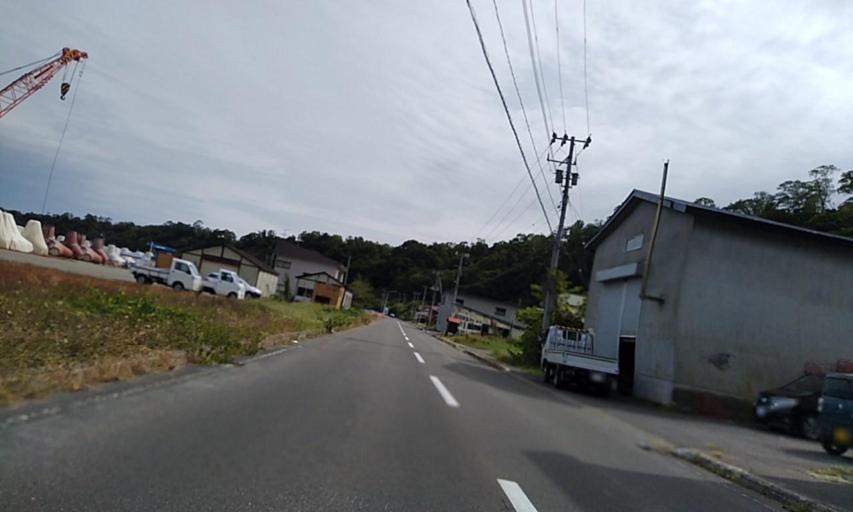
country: JP
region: Hokkaido
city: Rumoi
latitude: 43.8522
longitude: 141.5299
